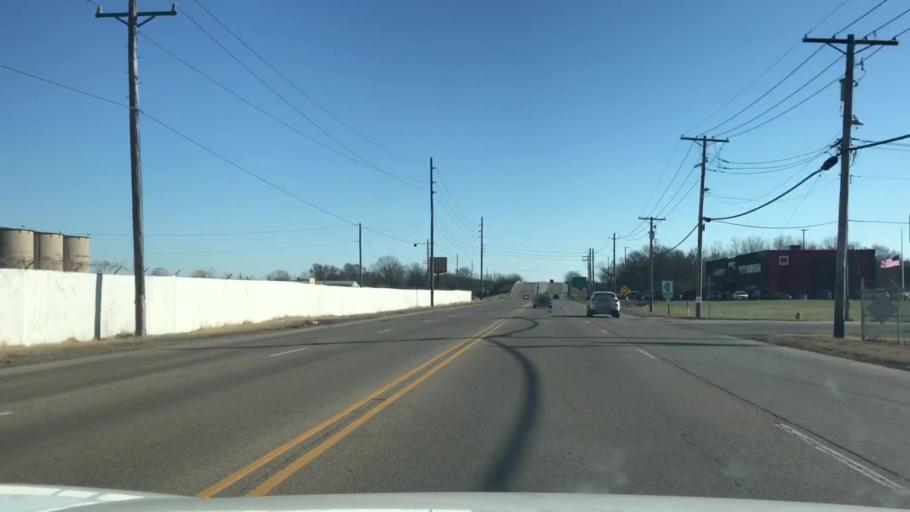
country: US
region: Illinois
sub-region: Saint Clair County
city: Alorton
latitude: 38.5970
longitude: -90.1246
